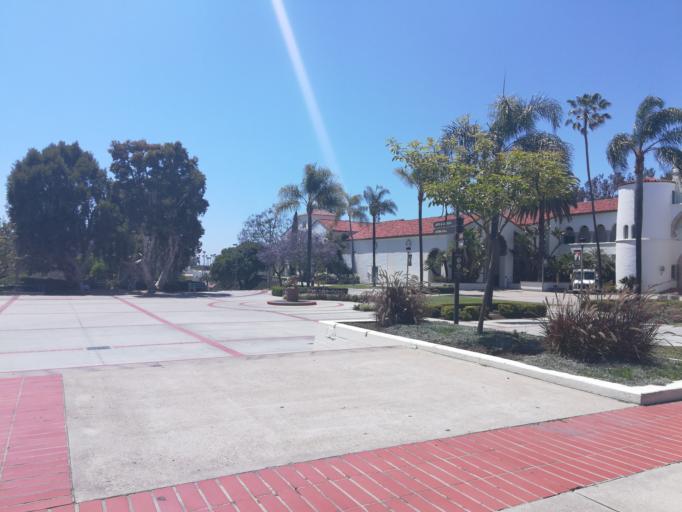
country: US
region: California
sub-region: San Diego County
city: La Mesa
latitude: 32.7758
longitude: -117.0716
